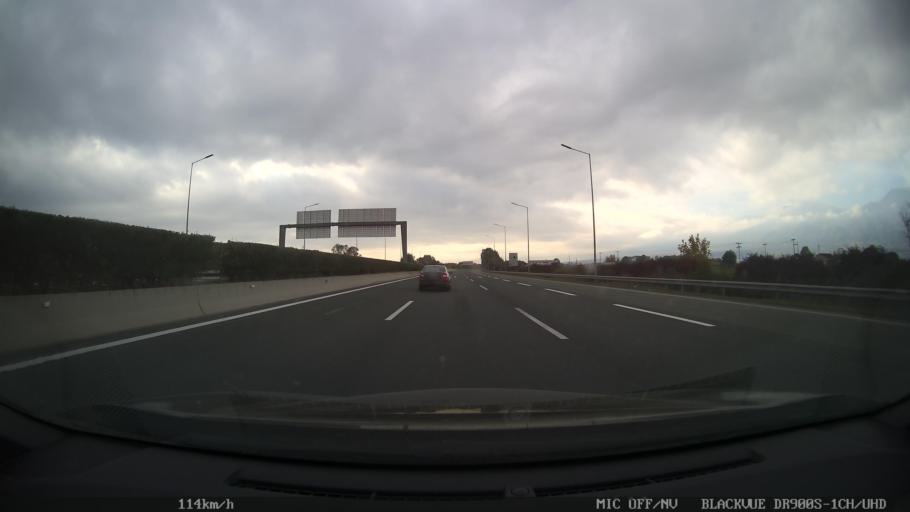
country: GR
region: Central Macedonia
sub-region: Nomos Pierias
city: Nea Efesos
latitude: 40.1904
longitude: 22.5500
